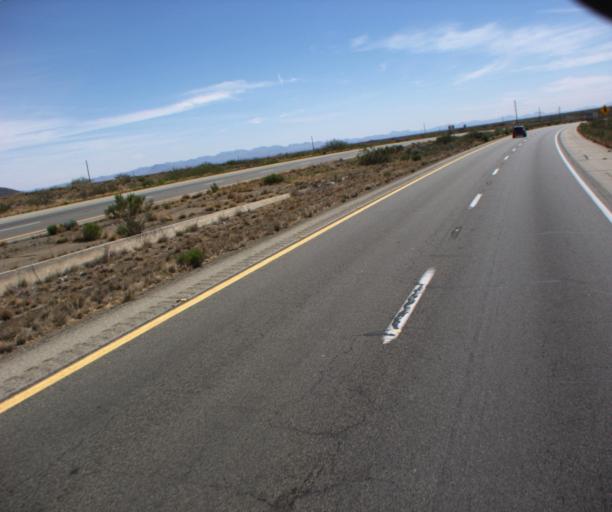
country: US
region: Arizona
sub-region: Cochise County
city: Willcox
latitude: 32.3616
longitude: -109.6191
